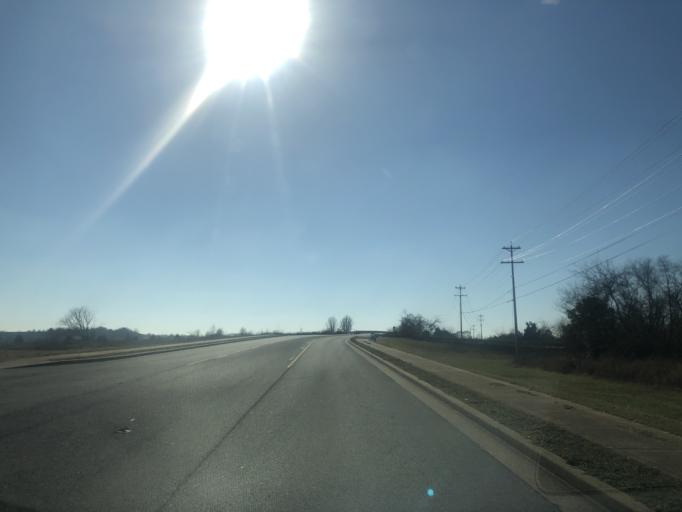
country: US
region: Tennessee
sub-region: Rutherford County
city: Smyrna
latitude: 35.8912
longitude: -86.4808
